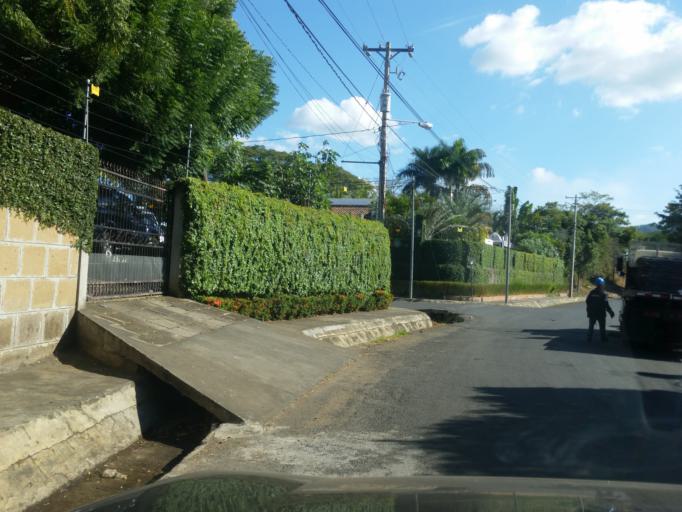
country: NI
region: Managua
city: Managua
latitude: 12.0747
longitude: -86.2365
